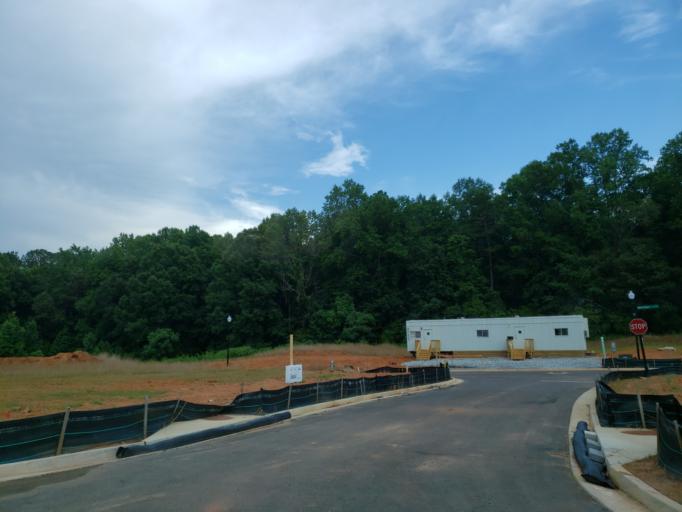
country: US
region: Georgia
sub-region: Cherokee County
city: Holly Springs
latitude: 34.1825
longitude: -84.4260
